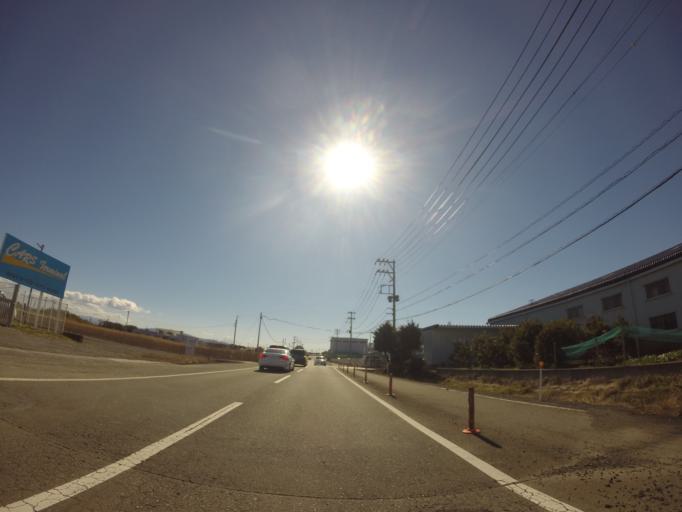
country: JP
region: Shizuoka
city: Fuji
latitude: 35.1461
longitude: 138.7409
